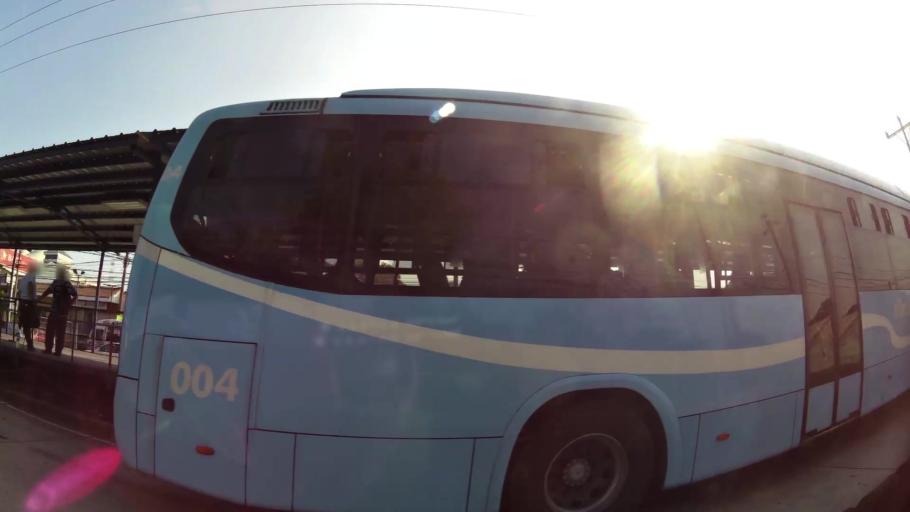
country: SV
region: San Salvador
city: Soyapango
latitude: 13.7003
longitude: -89.1527
